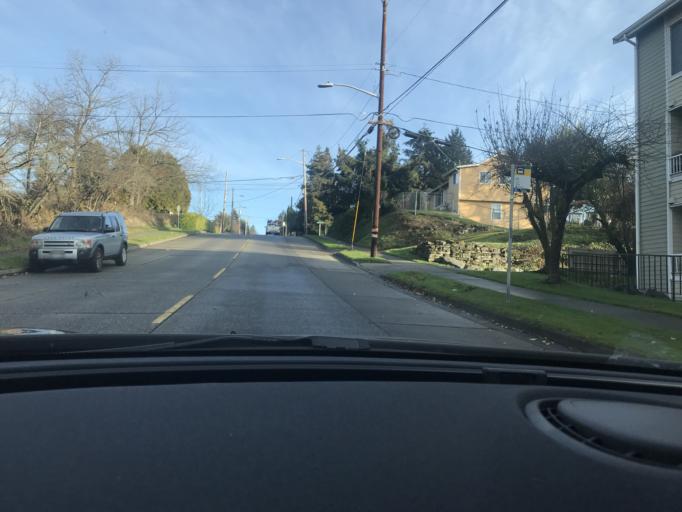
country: US
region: Washington
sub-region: King County
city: White Center
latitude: 47.5247
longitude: -122.3643
